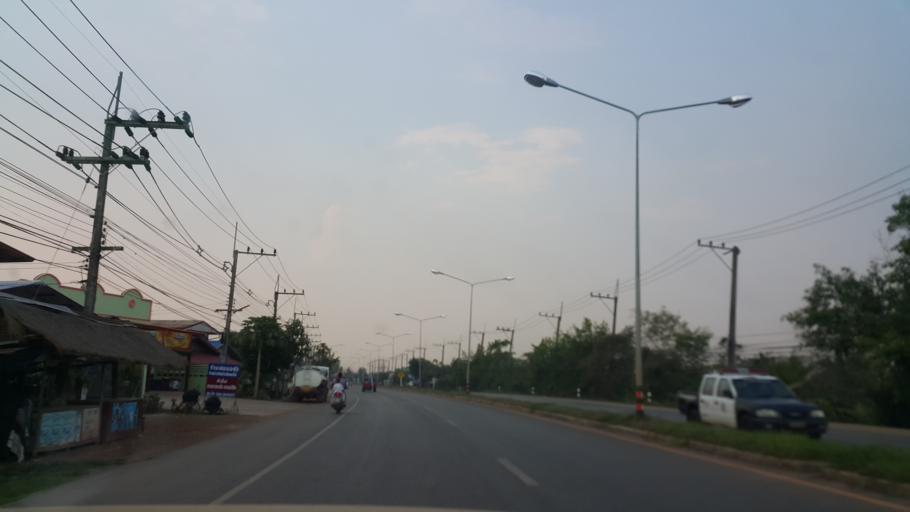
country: TH
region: Nakhon Phanom
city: That Phanom
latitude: 16.9885
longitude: 104.7262
